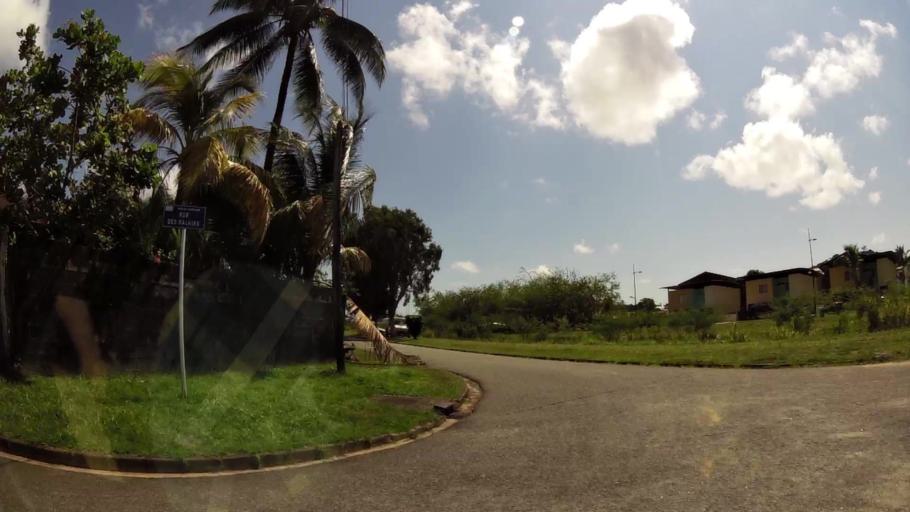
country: GF
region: Guyane
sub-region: Guyane
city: Cayenne
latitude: 4.9211
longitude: -52.3176
